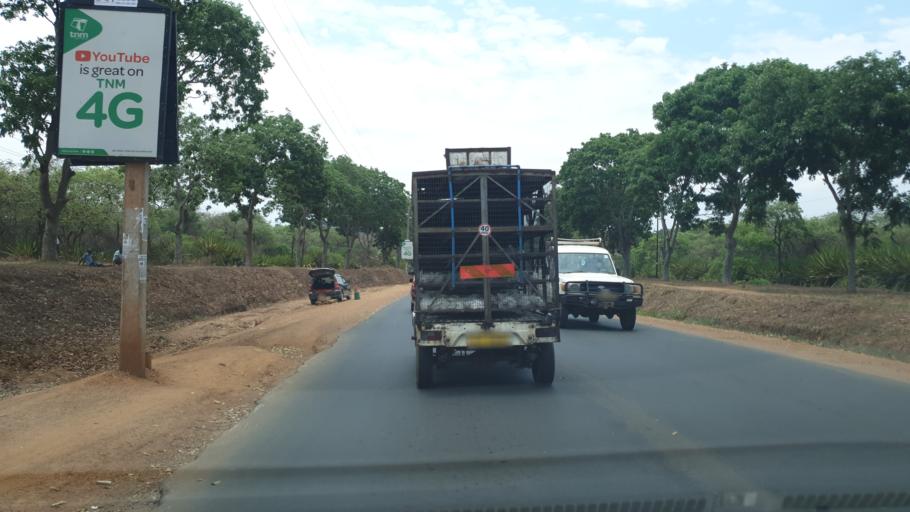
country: MW
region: Central Region
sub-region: Lilongwe District
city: Lilongwe
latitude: -13.9676
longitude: 33.7850
